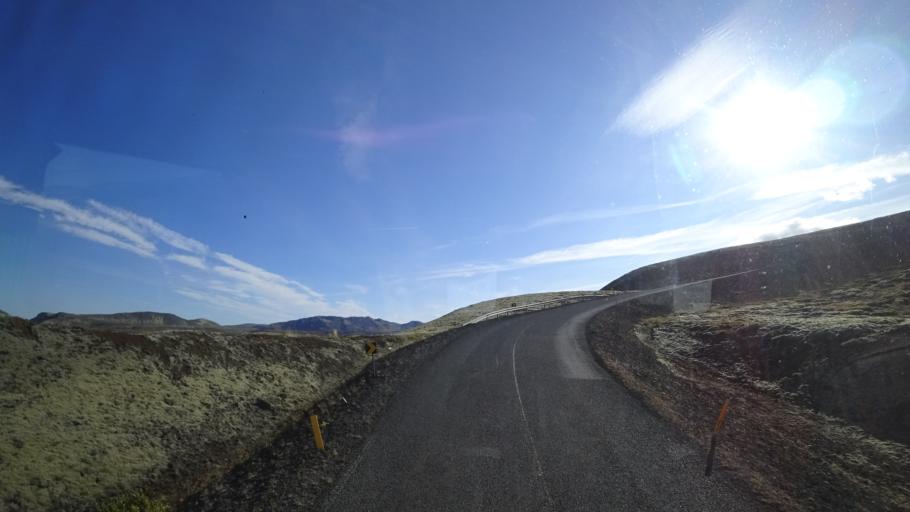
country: IS
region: South
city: Hveragerdi
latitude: 64.1180
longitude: -21.2610
